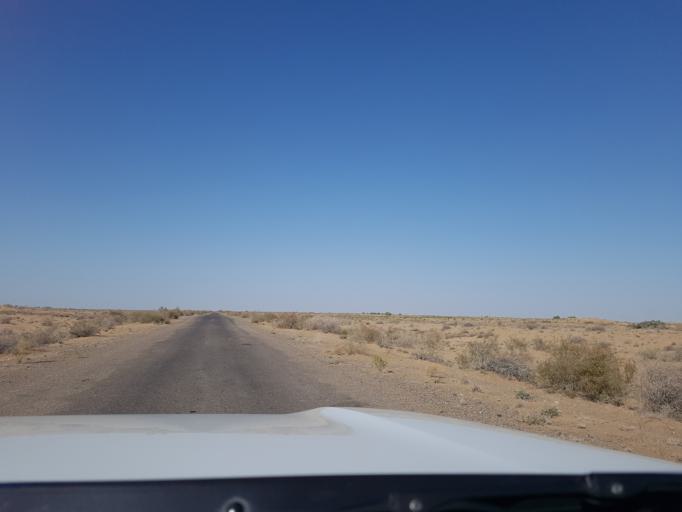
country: IR
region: Razavi Khorasan
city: Sarakhs
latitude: 36.7276
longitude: 61.3385
